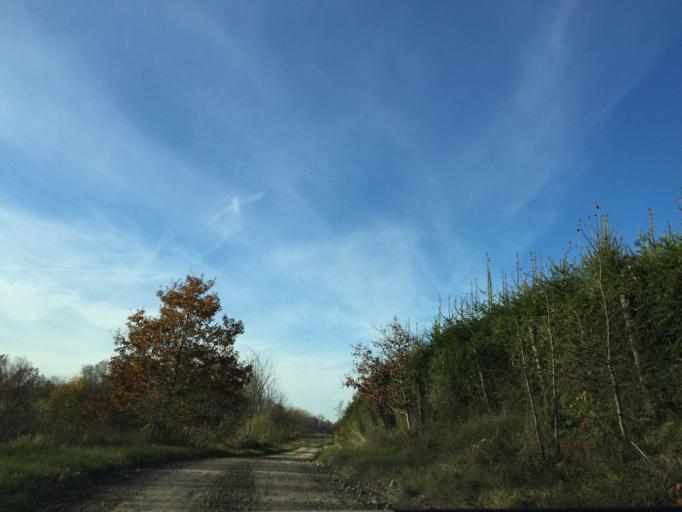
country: LV
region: Skriveri
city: Skriveri
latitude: 56.6172
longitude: 25.1512
